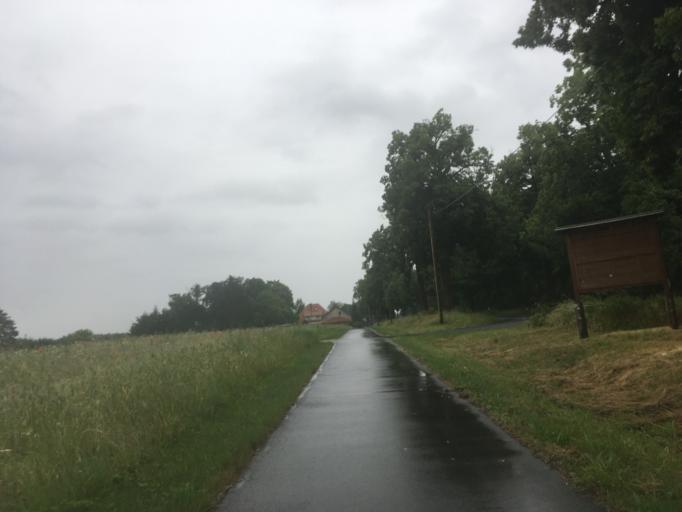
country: DE
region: Brandenburg
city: Marienwerder
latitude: 52.9201
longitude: 13.5424
